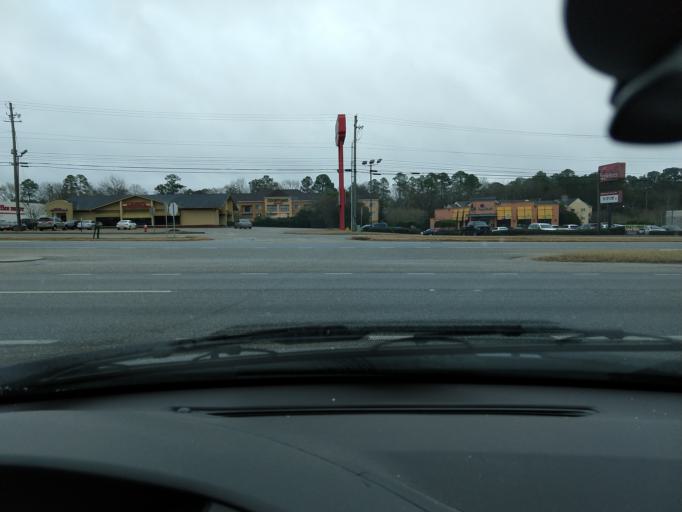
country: US
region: Alabama
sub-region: Houston County
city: Dothan
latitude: 31.2245
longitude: -85.4325
